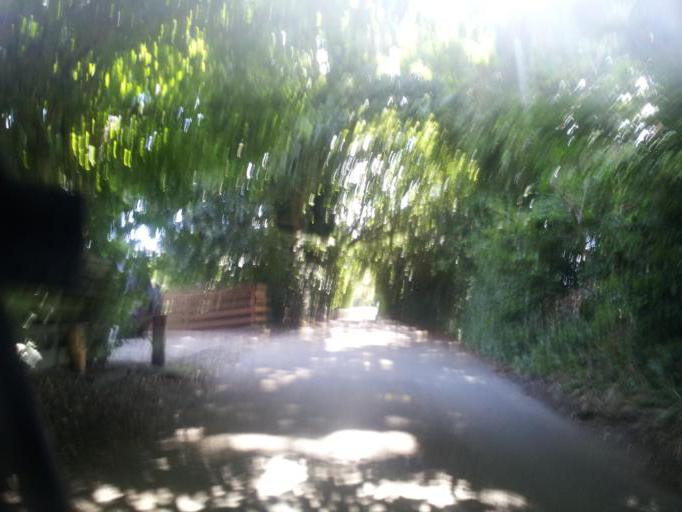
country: GB
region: England
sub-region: Kent
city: Lenham
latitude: 51.2873
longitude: 0.7014
